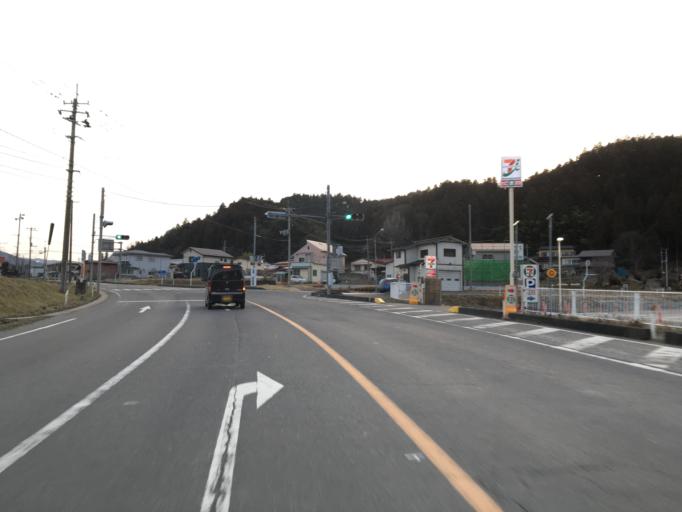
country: JP
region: Fukushima
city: Ishikawa
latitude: 37.0263
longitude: 140.3593
